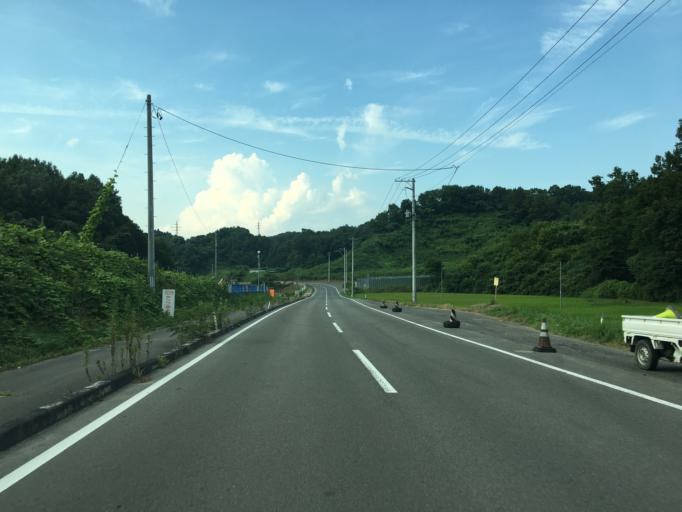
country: JP
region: Fukushima
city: Nihommatsu
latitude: 37.5458
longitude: 140.4416
